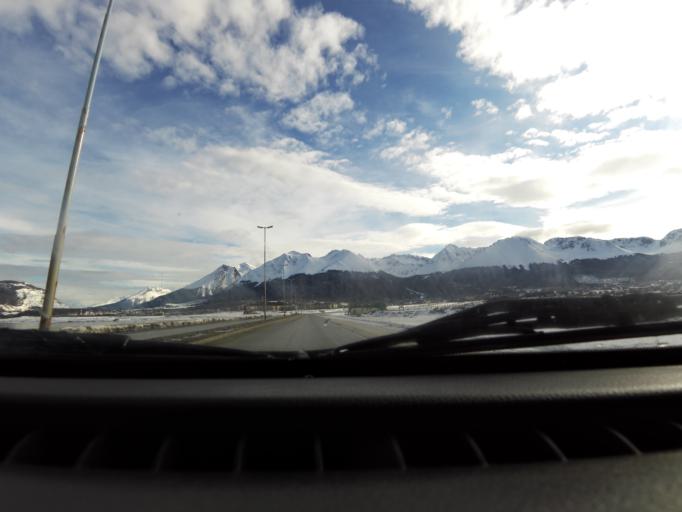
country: AR
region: Tierra del Fuego
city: Ushuaia
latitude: -54.8320
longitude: -68.3233
